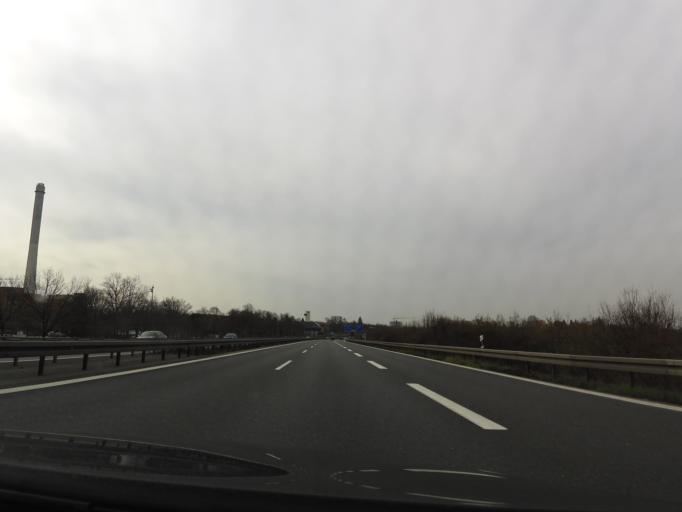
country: DE
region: Bavaria
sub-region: Regierungsbezirk Mittelfranken
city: Erlangen
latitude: 49.5969
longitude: 10.9981
